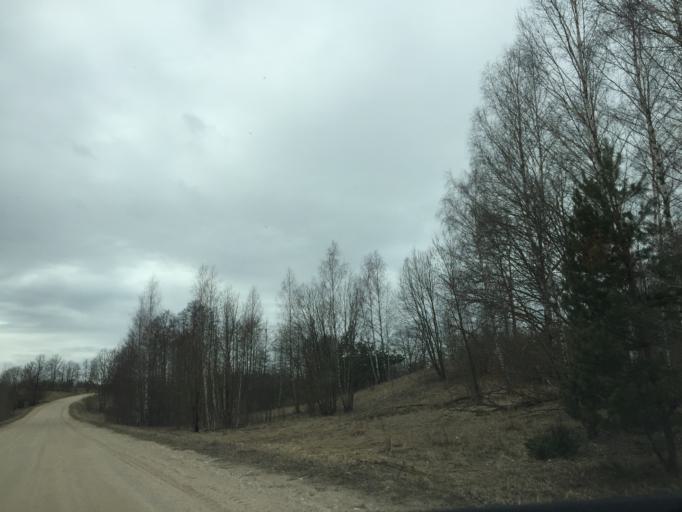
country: LV
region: Kraslavas Rajons
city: Kraslava
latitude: 55.9815
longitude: 27.1063
